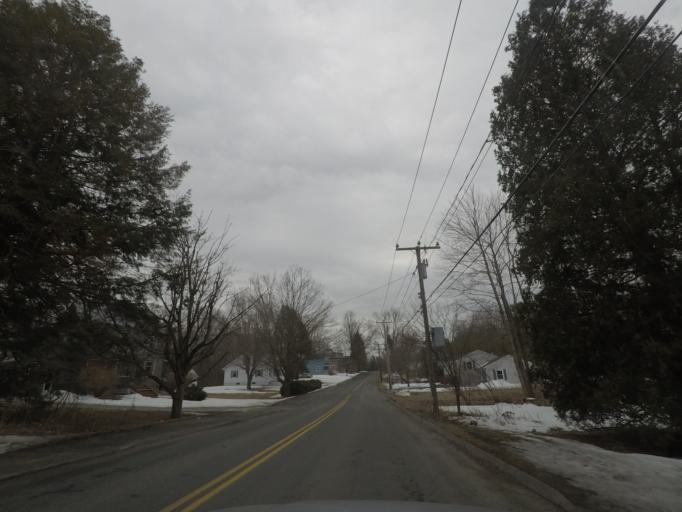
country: US
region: Massachusetts
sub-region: Berkshire County
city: Lee
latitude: 42.3095
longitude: -73.2566
